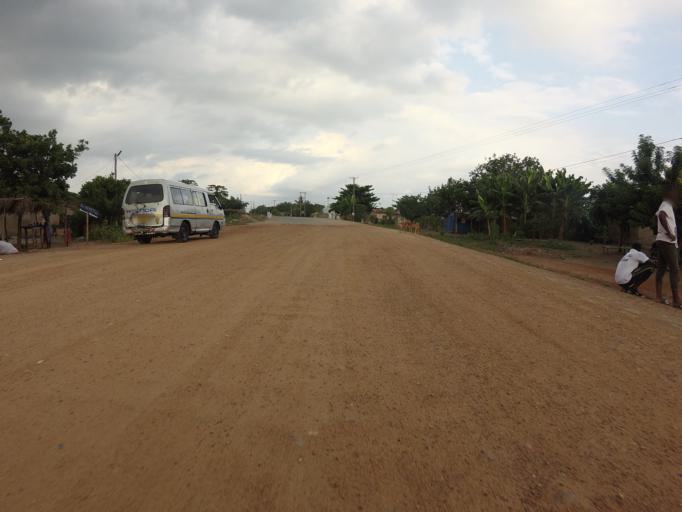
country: GH
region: Volta
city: Ho
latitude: 6.4272
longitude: 0.5114
